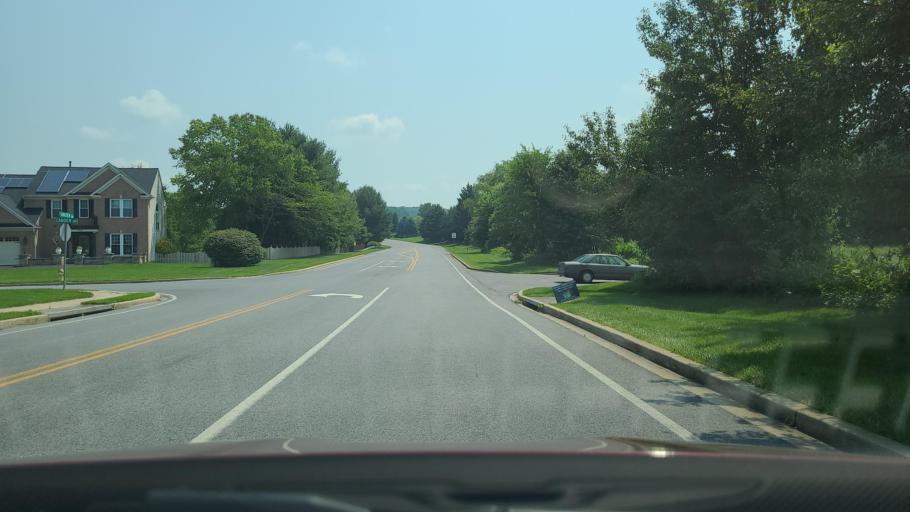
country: US
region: Maryland
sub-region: Frederick County
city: Jefferson
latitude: 39.3640
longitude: -77.5293
